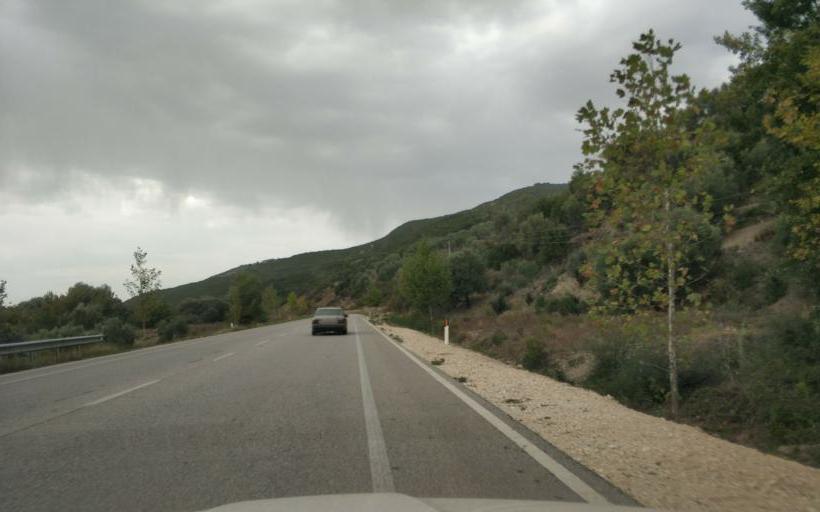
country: AL
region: Fier
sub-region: Rrethi i Mallakastres
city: Hekal
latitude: 40.5228
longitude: 19.7391
